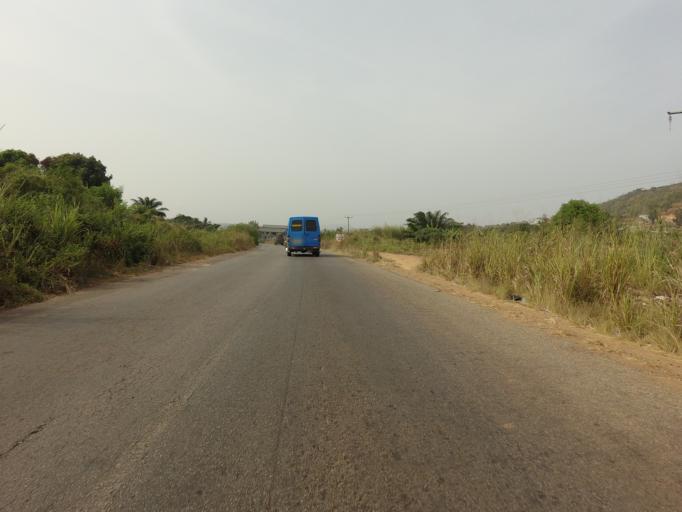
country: GH
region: Volta
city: Ho
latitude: 6.6069
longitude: 0.4538
